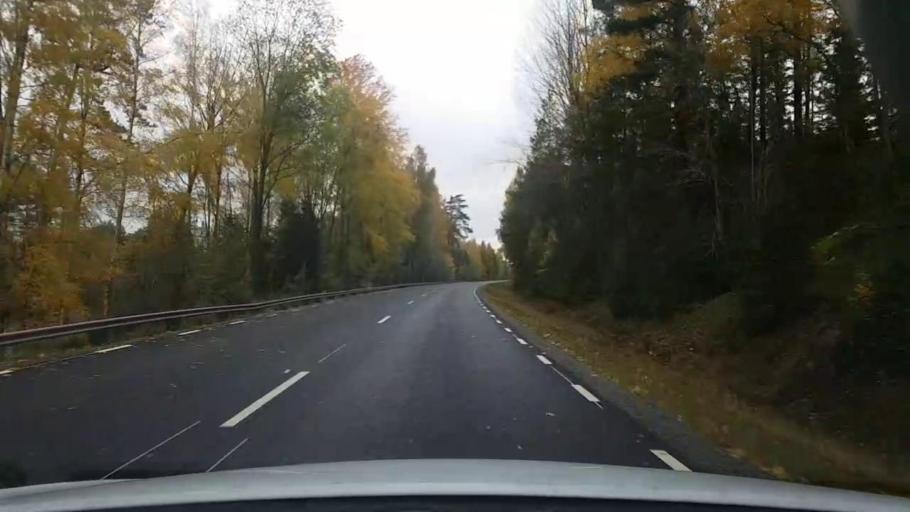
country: SE
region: OErebro
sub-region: Laxa Kommun
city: Laxa
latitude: 58.8245
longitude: 14.5465
